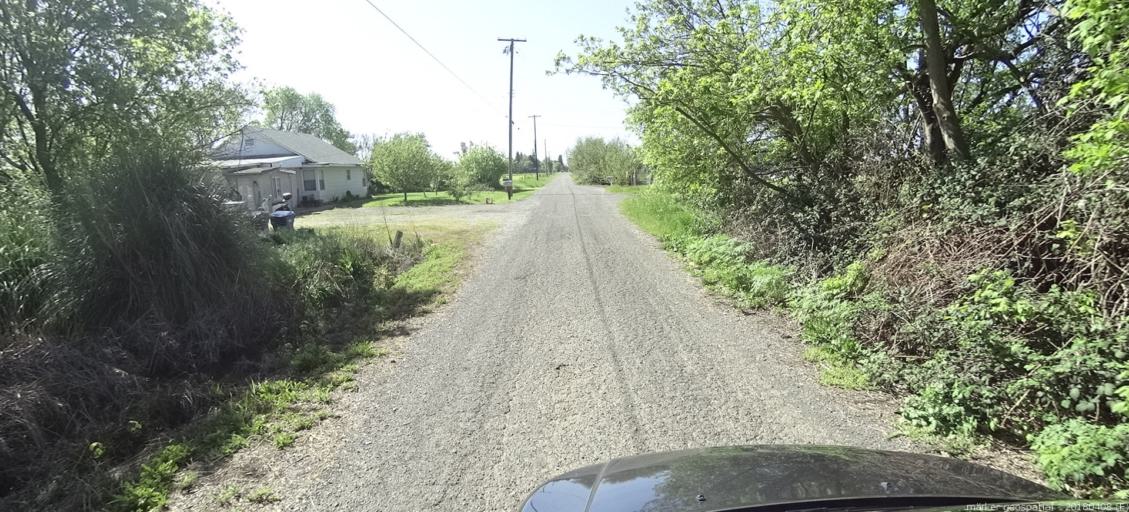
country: US
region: California
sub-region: Sacramento County
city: Laguna
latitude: 38.3398
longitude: -121.4638
